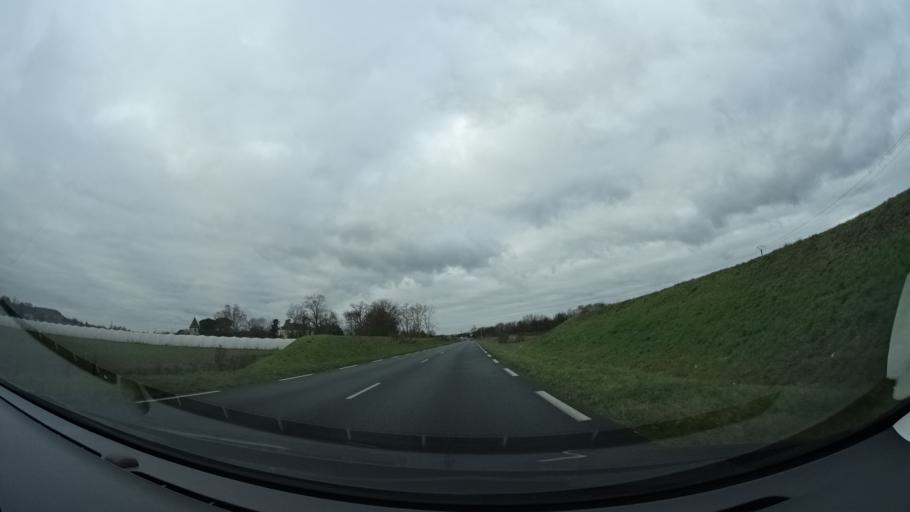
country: FR
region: Aquitaine
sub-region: Departement du Lot-et-Garonne
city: Pujols
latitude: 44.3987
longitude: 0.6789
